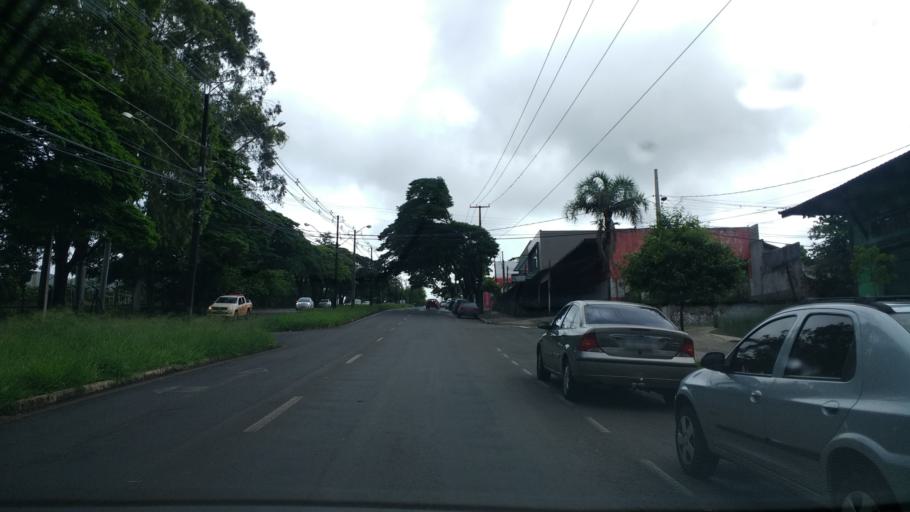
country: BR
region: Parana
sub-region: Londrina
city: Londrina
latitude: -23.3134
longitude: -51.2075
